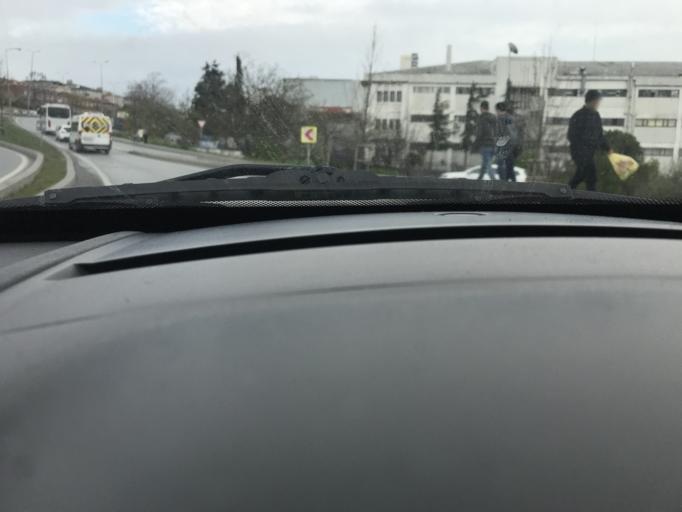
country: TR
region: Istanbul
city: Yakuplu
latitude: 40.9975
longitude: 28.7000
